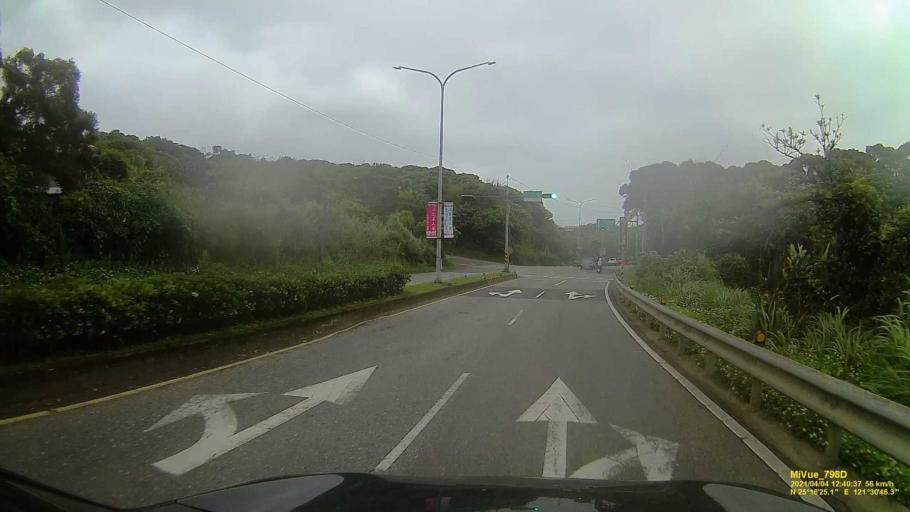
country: TW
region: Taipei
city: Taipei
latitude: 25.2734
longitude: 121.5127
